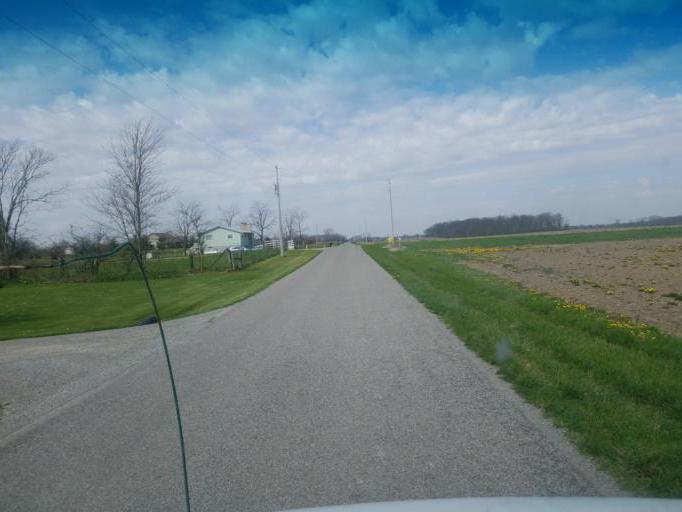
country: US
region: Ohio
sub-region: Logan County
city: Northwood
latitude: 40.4927
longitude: -83.7157
